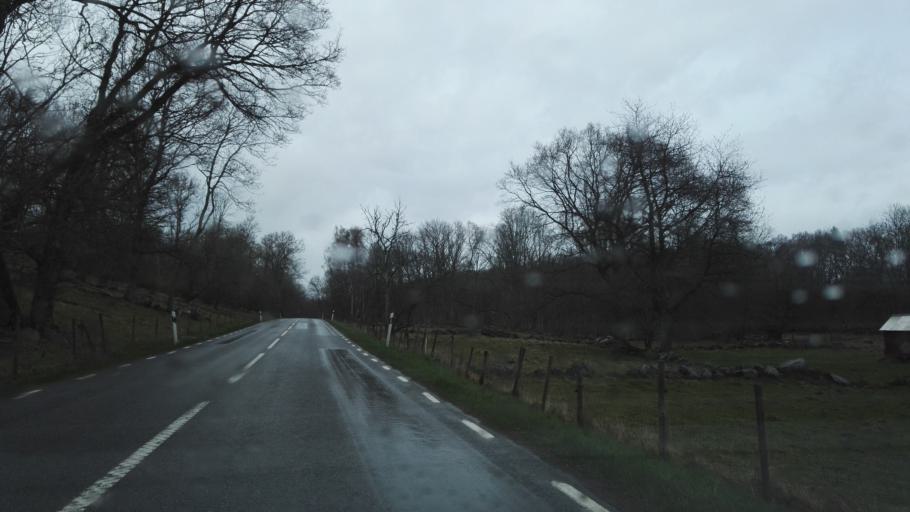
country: SE
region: Skane
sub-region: Simrishamns Kommun
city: Kivik
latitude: 55.6521
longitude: 14.2191
